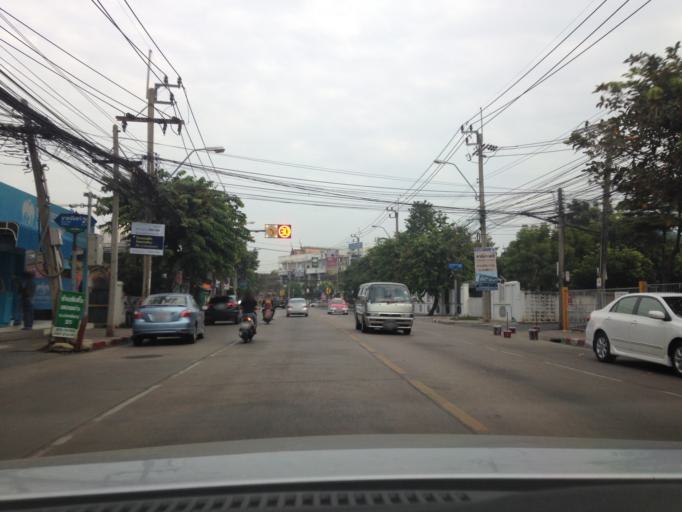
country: TH
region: Bangkok
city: Khan Na Yao
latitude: 13.8338
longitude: 100.6377
